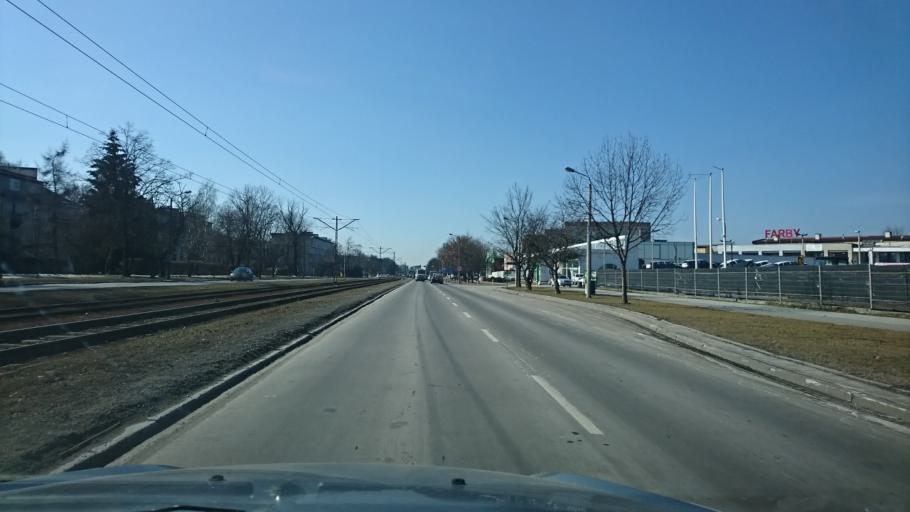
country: PL
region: Lesser Poland Voivodeship
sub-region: Powiat wielicki
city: Kokotow
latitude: 50.0839
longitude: 20.0356
